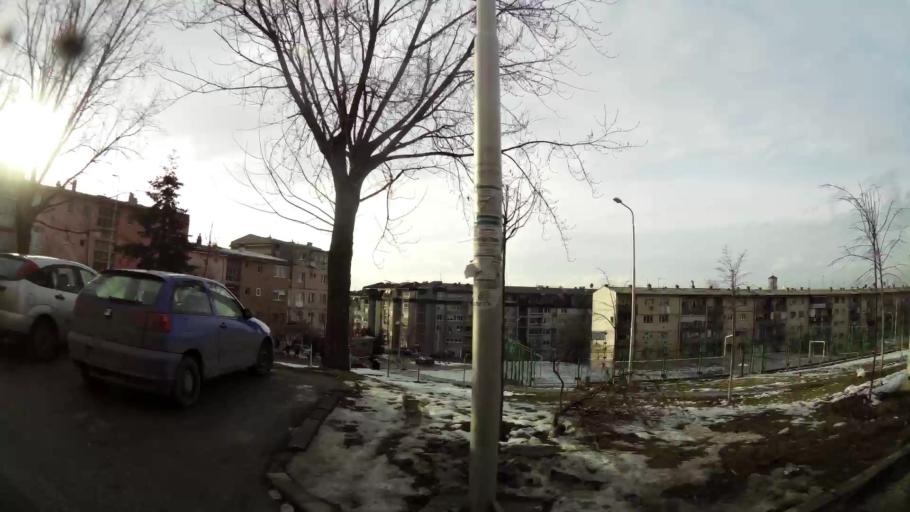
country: XK
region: Pristina
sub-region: Komuna e Prishtines
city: Pristina
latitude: 42.6529
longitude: 21.1630
